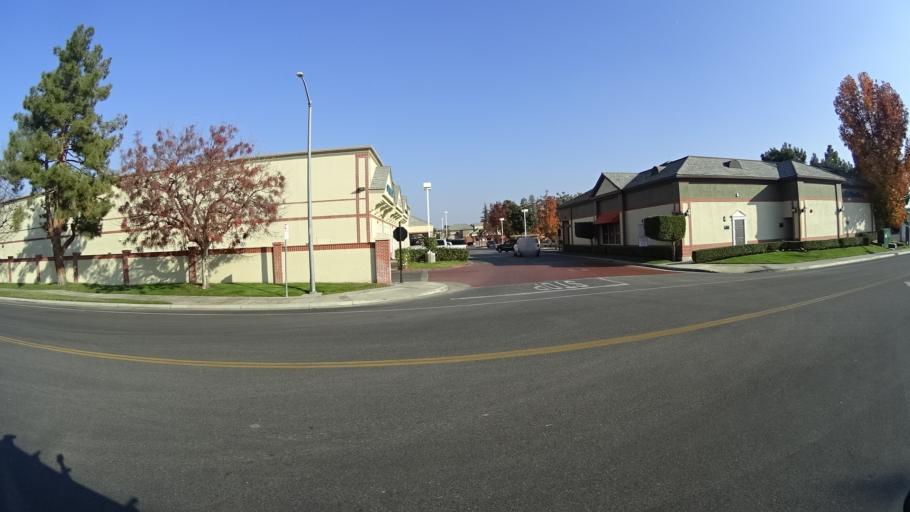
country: US
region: California
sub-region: Kern County
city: Greenacres
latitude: 35.3404
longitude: -119.1062
